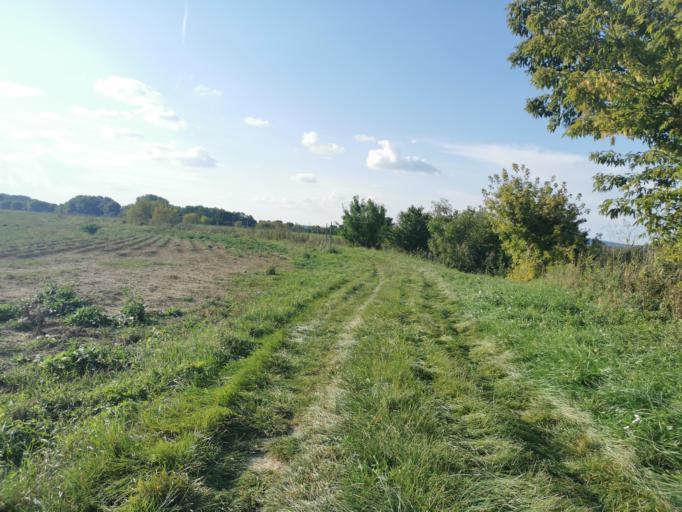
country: SK
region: Trnavsky
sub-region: Okres Senica
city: Senica
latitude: 48.6626
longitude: 17.3098
